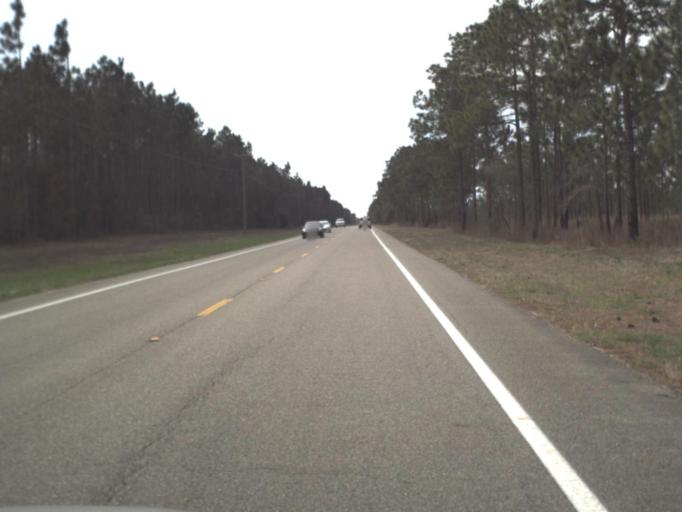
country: US
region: Florida
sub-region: Liberty County
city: Bristol
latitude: 30.4679
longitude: -84.9423
